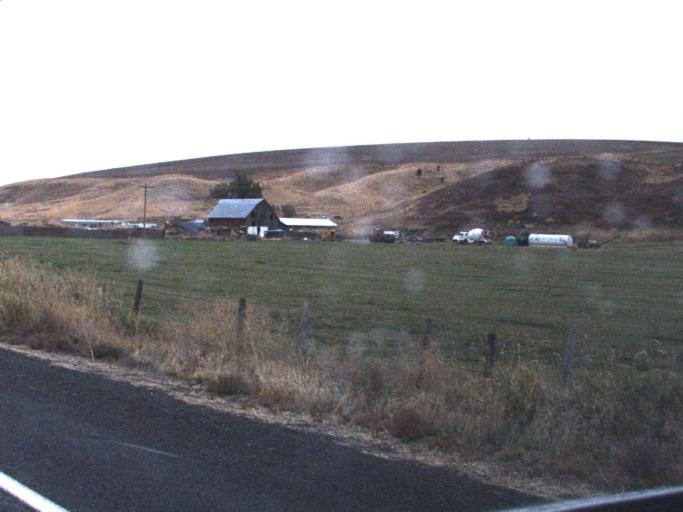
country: US
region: Washington
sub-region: Whitman County
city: Colfax
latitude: 46.8105
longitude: -117.5851
